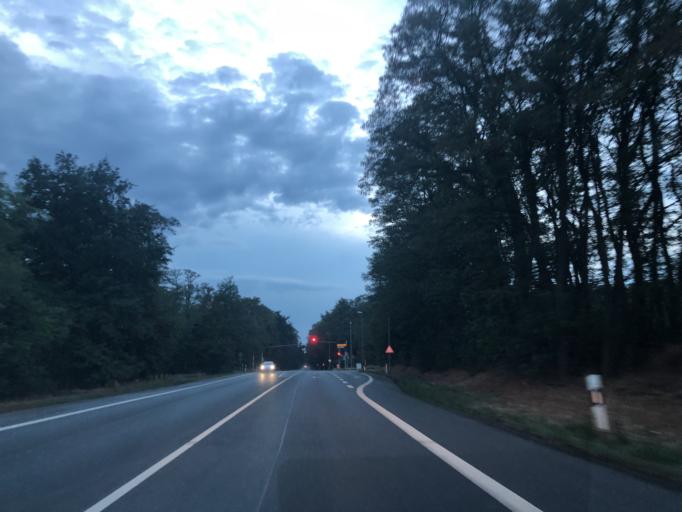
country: DE
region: Hesse
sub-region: Regierungsbezirk Darmstadt
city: Nauheim
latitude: 49.9433
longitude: 8.4415
